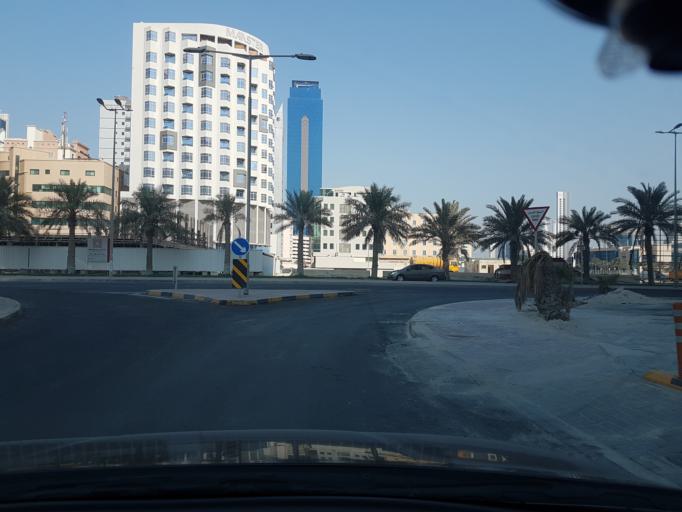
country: BH
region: Manama
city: Jidd Hafs
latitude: 26.2357
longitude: 50.5368
